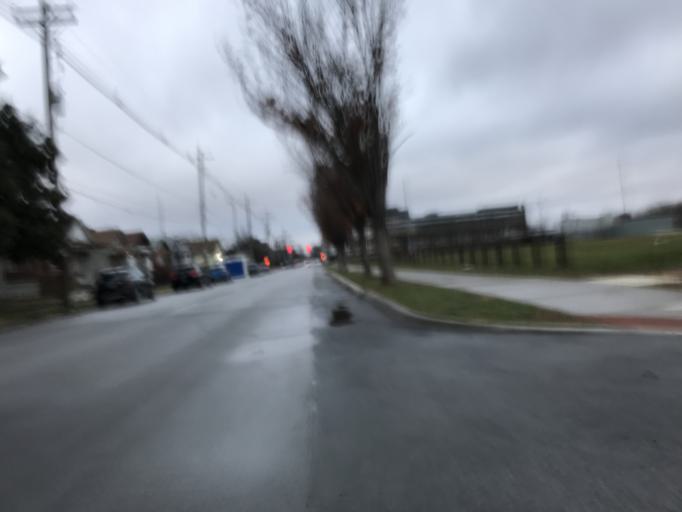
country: US
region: Kentucky
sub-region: Jefferson County
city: Louisville
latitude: 38.2384
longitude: -85.7393
